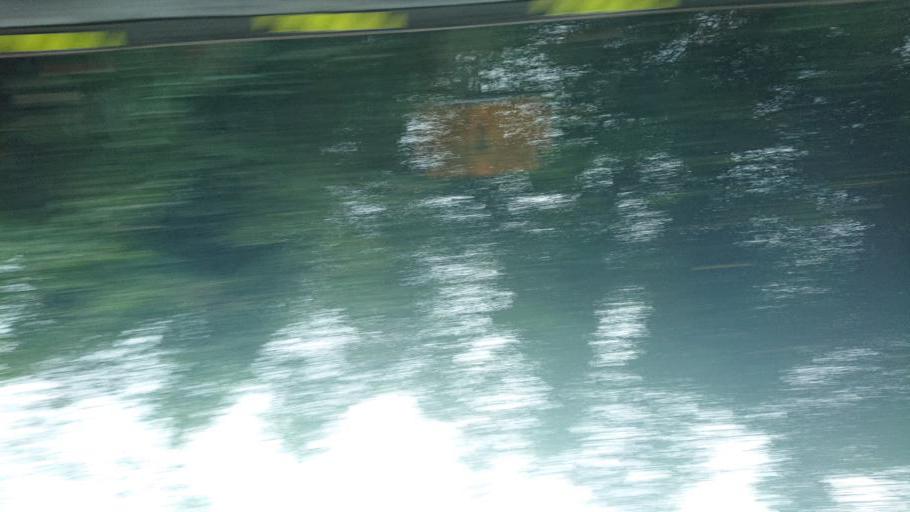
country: TW
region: Taiwan
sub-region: Chiayi
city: Jiayi Shi
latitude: 23.4690
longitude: 120.7184
